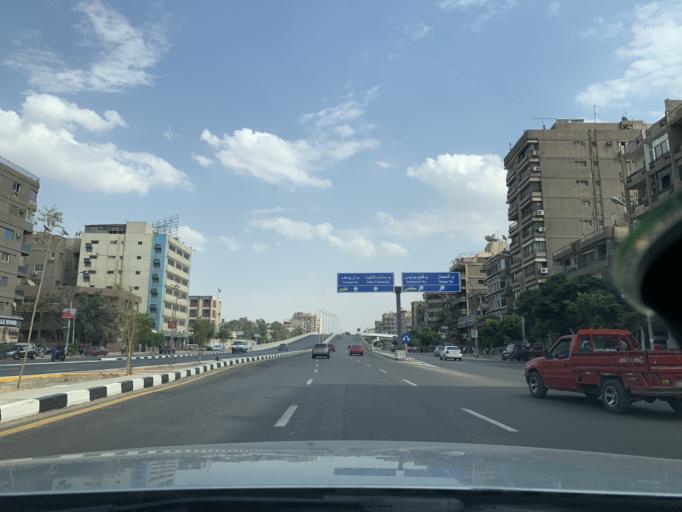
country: EG
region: Muhafazat al Qalyubiyah
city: Al Khankah
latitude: 30.1139
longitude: 31.3439
